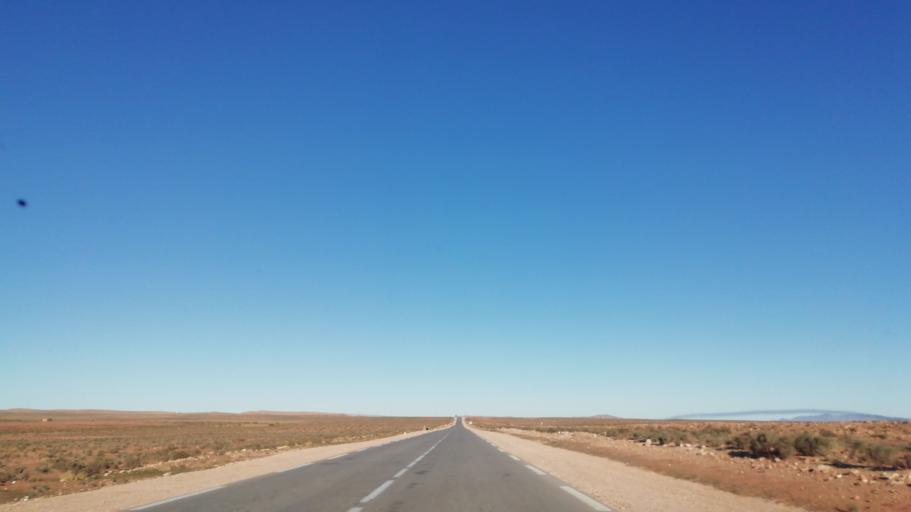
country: DZ
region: El Bayadh
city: El Abiodh Sidi Cheikh
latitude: 33.1194
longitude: 0.2720
